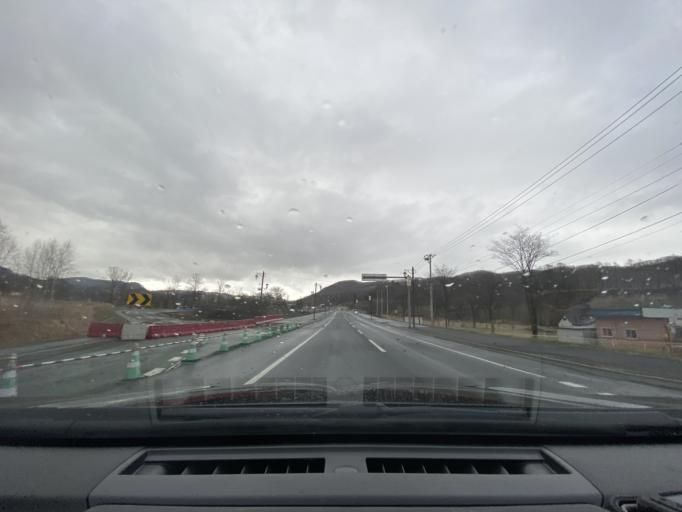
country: JP
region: Hokkaido
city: Otofuke
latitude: 43.2526
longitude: 143.5476
